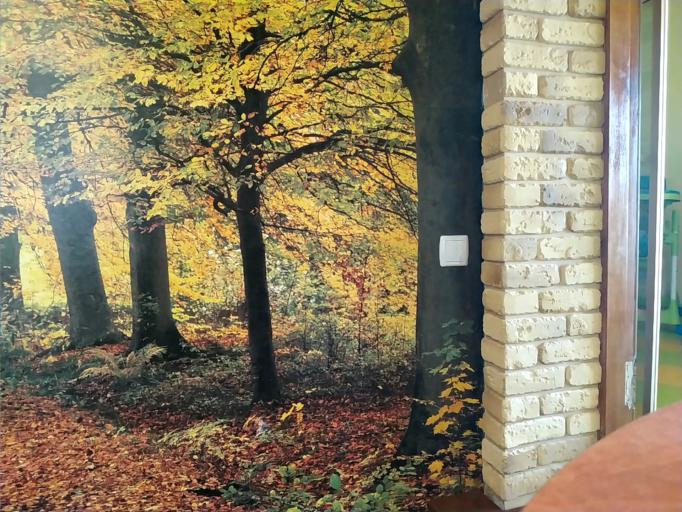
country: RU
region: Tverskaya
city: Maksatikha
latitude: 57.6131
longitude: 35.8467
